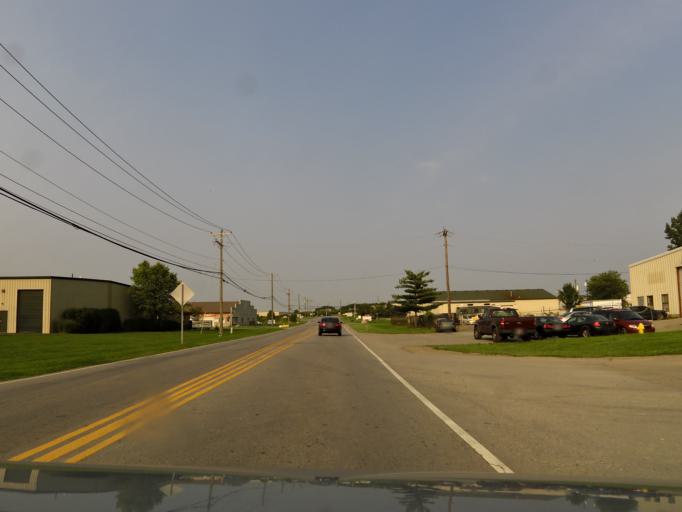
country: US
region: Ohio
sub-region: Hamilton County
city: Forest Park
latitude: 39.3350
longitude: -84.5080
